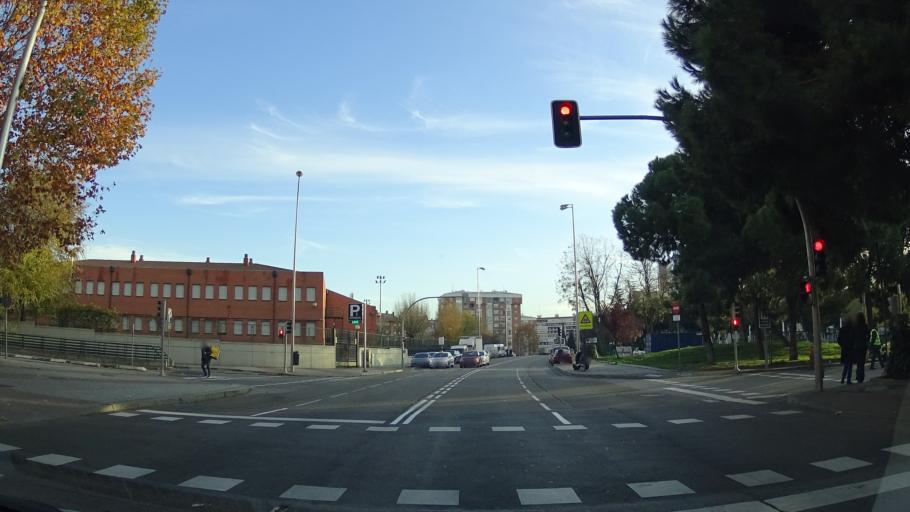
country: ES
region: Madrid
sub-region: Provincia de Madrid
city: Ciudad Lineal
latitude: 40.4399
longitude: -3.6570
